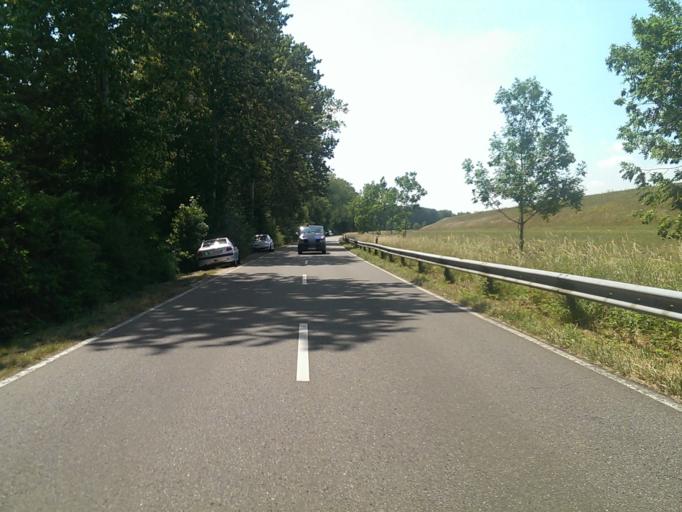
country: DE
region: Baden-Wuerttemberg
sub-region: Karlsruhe Region
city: Hugelsheim
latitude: 48.7893
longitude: 8.0706
